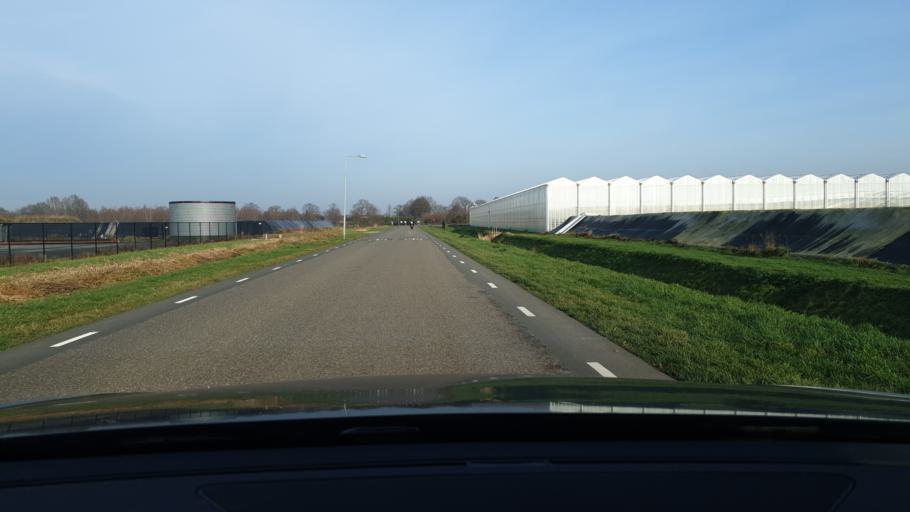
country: NL
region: Limburg
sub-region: Gemeente Peel en Maas
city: Maasbree
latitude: 51.4318
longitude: 6.0826
